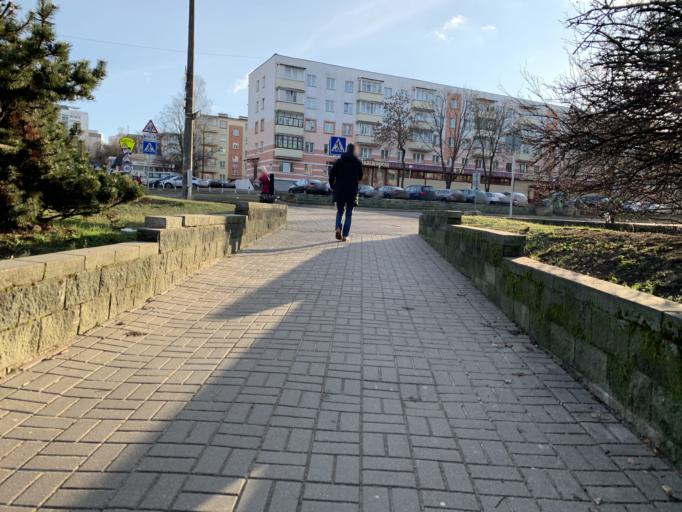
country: BY
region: Minsk
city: Minsk
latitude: 53.9134
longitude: 27.5863
